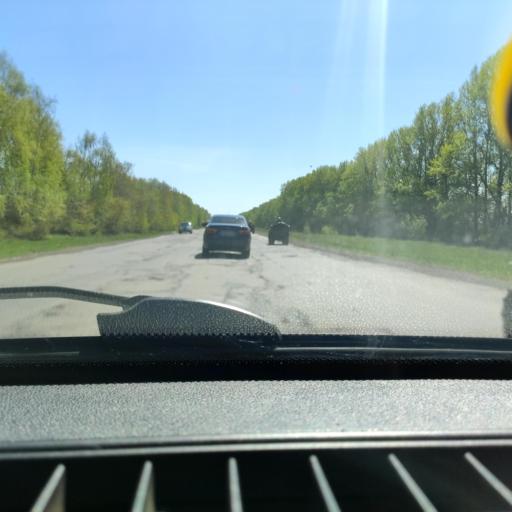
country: RU
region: Samara
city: Tol'yatti
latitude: 53.6439
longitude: 49.4210
